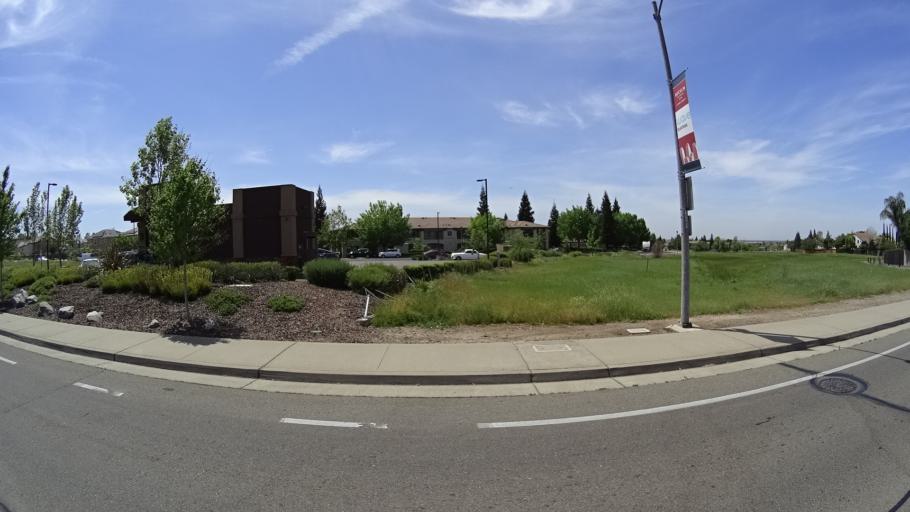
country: US
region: California
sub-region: Placer County
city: Rocklin
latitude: 38.7983
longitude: -121.2675
